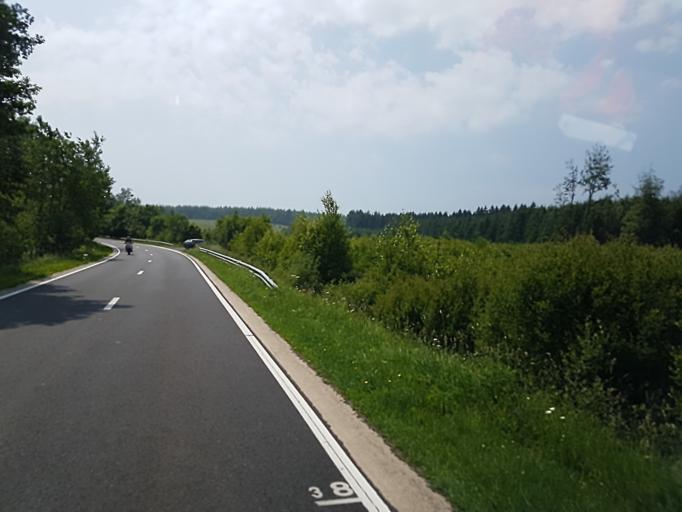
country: BE
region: Wallonia
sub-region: Province de Liege
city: Lierneux
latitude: 50.3382
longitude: 5.7890
